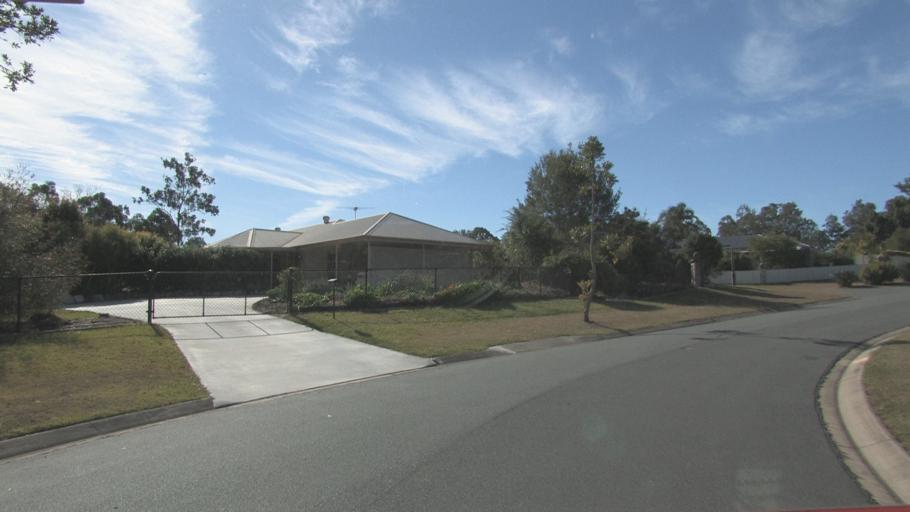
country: AU
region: Queensland
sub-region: Logan
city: North Maclean
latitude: -27.8122
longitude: 152.9582
